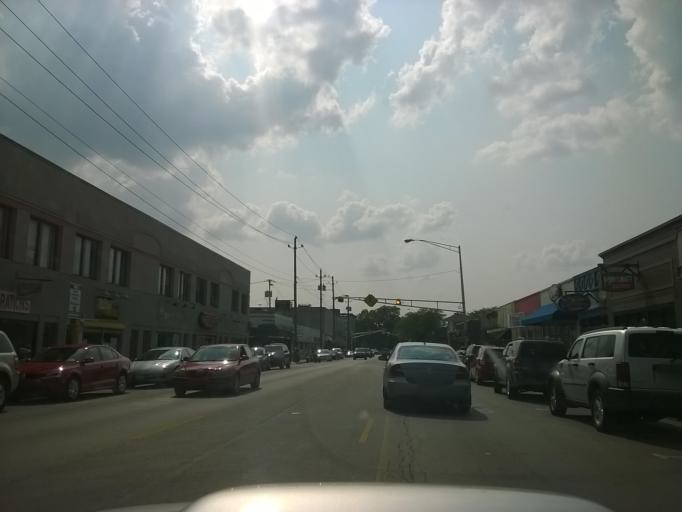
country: US
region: Indiana
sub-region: Marion County
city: Broad Ripple
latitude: 39.8698
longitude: -86.1441
